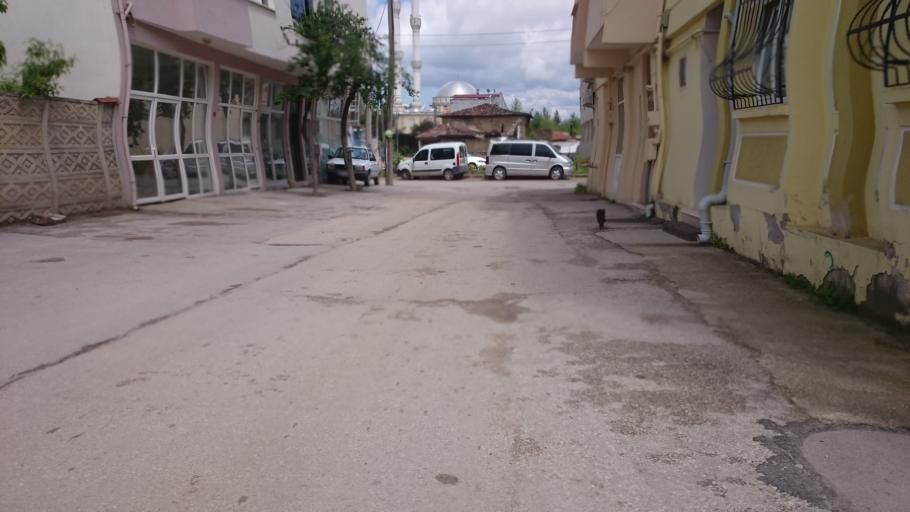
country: TR
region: Bursa
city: Niluefer
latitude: 40.2367
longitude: 28.9082
